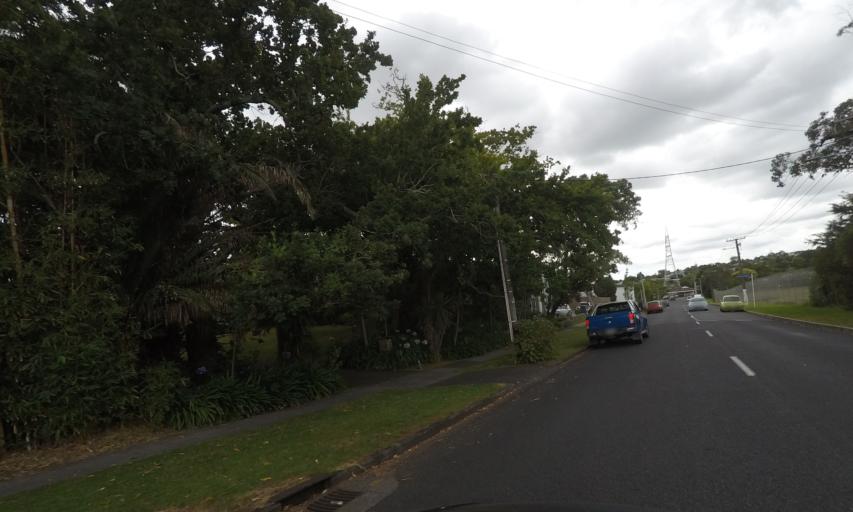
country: NZ
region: Auckland
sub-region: Auckland
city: Waitakere
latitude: -36.9169
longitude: 174.6886
